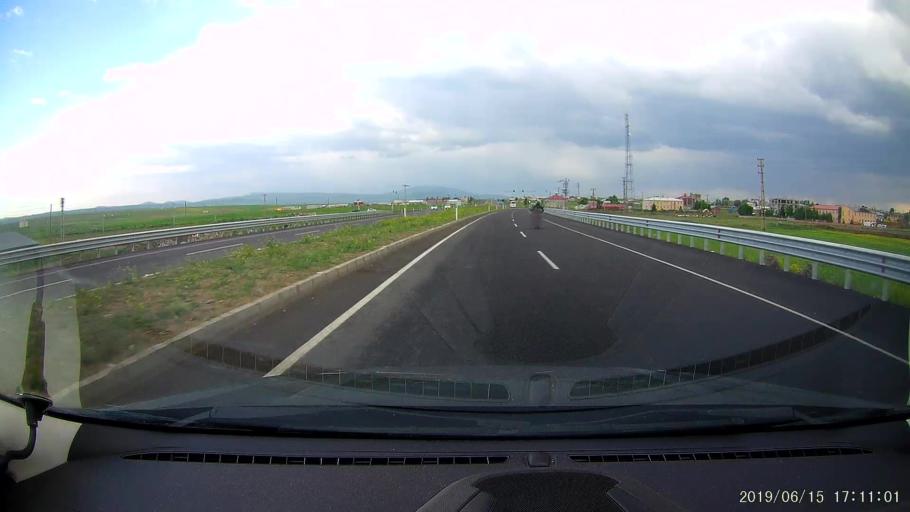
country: TR
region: Kars
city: Kars
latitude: 40.6156
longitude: 43.1334
